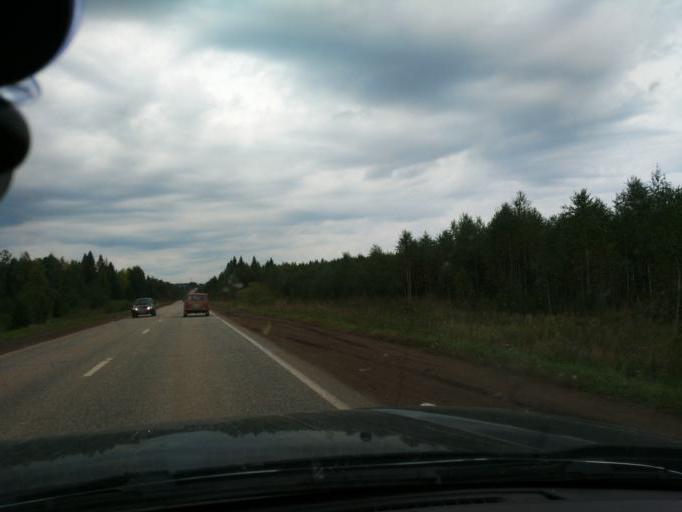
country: RU
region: Perm
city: Chernushka
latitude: 56.8048
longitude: 56.0626
